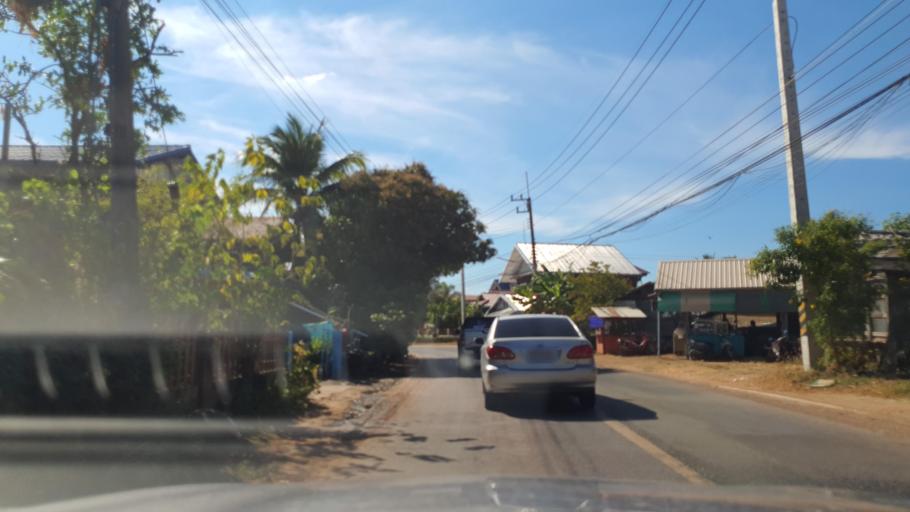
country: TH
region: Kalasin
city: Khao Wong
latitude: 16.7377
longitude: 104.1014
